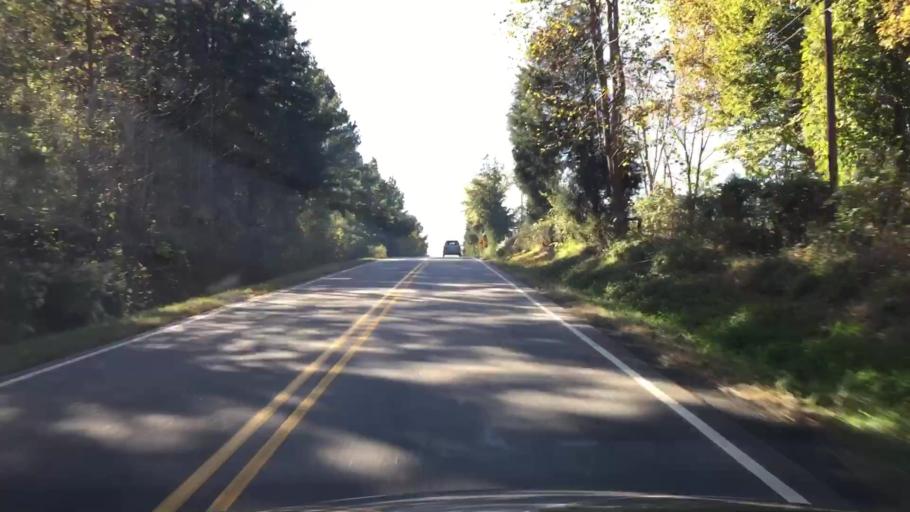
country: US
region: North Carolina
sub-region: Iredell County
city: Mooresville
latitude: 35.6200
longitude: -80.7250
